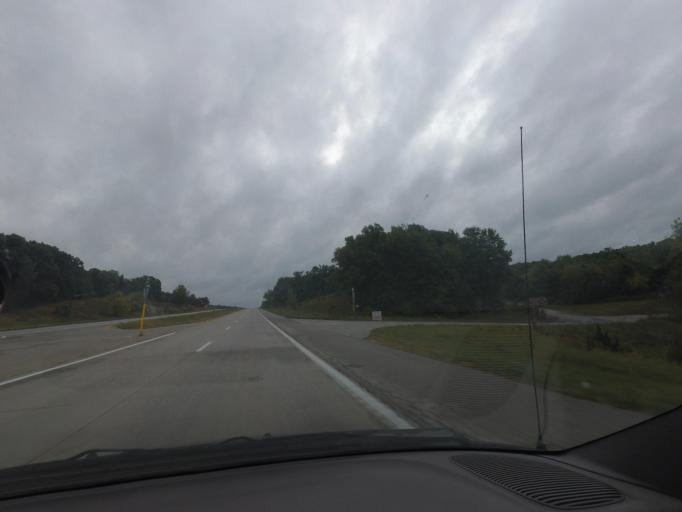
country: US
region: Missouri
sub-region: Shelby County
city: Shelbina
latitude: 39.6692
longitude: -91.9009
